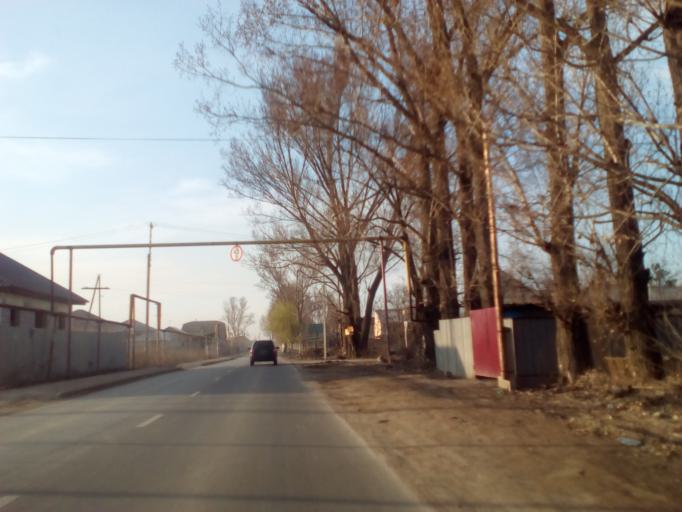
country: KZ
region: Almaty Oblysy
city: Burunday
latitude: 43.2419
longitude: 76.7884
